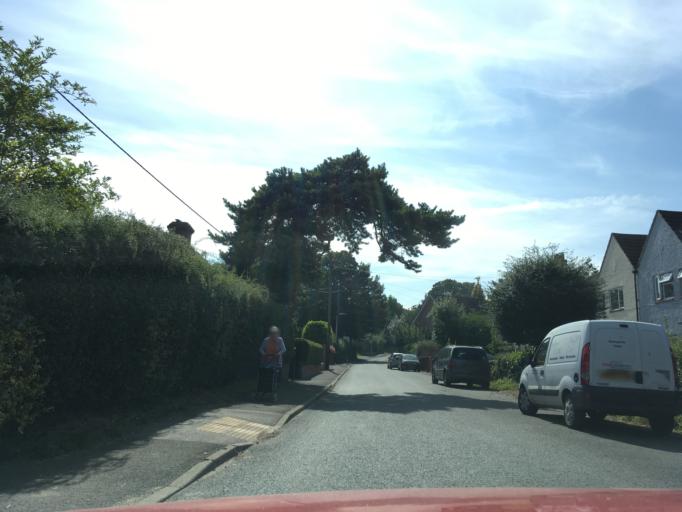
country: GB
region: England
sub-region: West Berkshire
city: Kintbury
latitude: 51.3962
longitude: -1.4485
